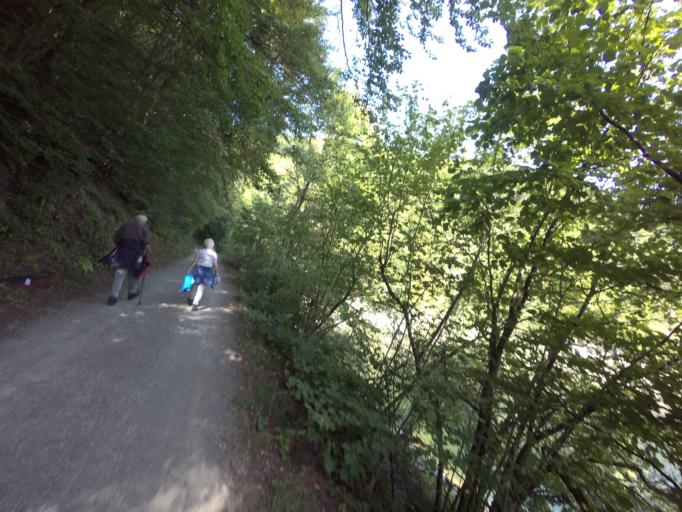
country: DE
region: North Rhine-Westphalia
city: Heimbach
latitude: 50.6504
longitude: 6.4183
